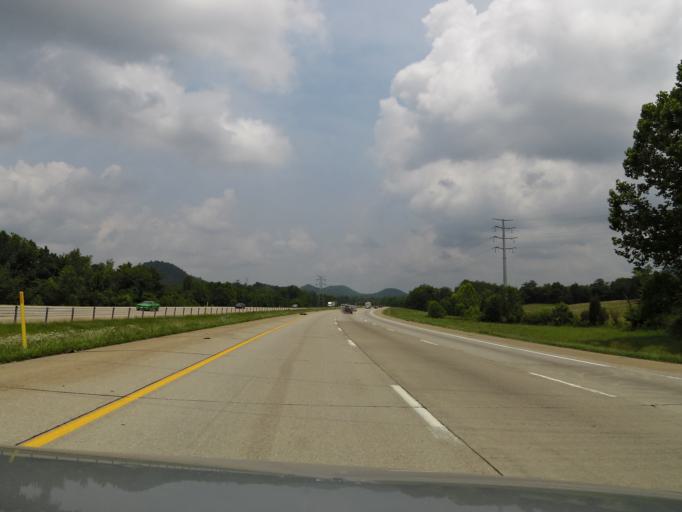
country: US
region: Kentucky
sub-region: Bullitt County
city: Lebanon Junction
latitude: 37.8501
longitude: -85.7137
